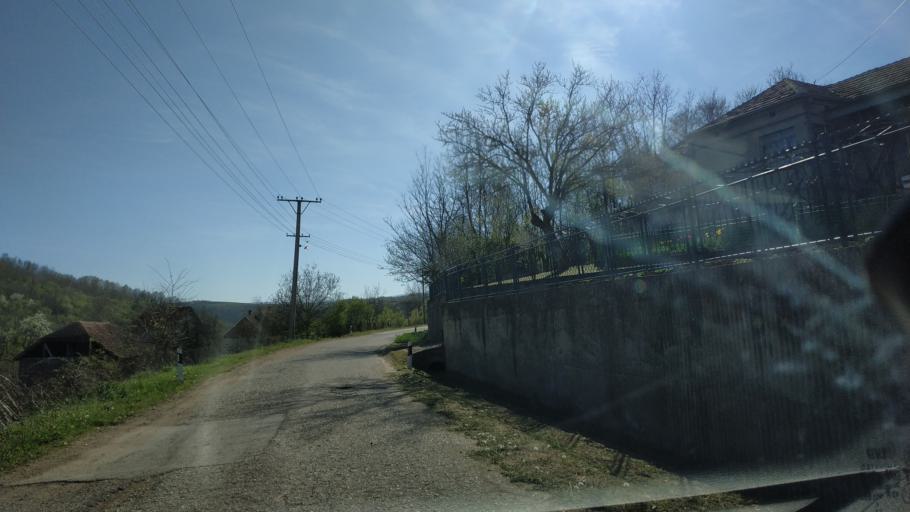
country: RS
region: Central Serbia
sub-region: Nisavski Okrug
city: Aleksinac
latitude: 43.4766
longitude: 21.6504
